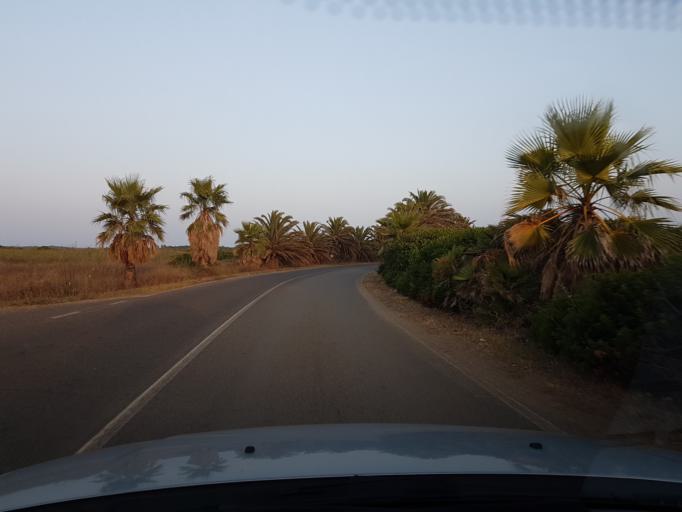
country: IT
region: Sardinia
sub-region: Provincia di Oristano
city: Cabras
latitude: 39.9520
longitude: 8.4091
